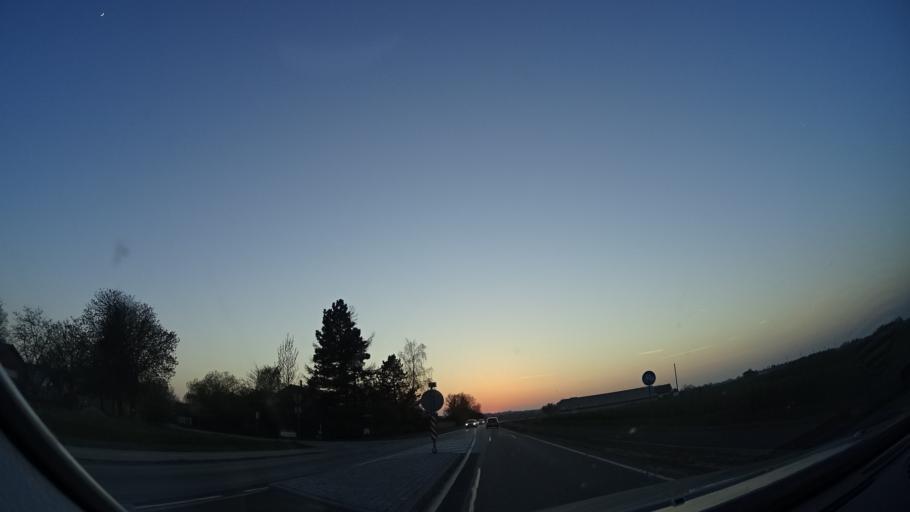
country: DK
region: Zealand
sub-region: Lejre Kommune
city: Ejby
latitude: 55.6580
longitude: 11.9126
